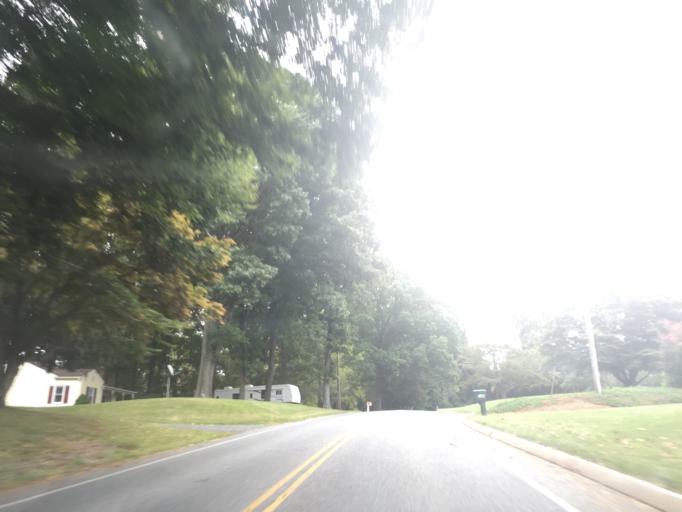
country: US
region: Maryland
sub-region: Harford County
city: Bel Air South
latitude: 39.5038
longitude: -76.3377
